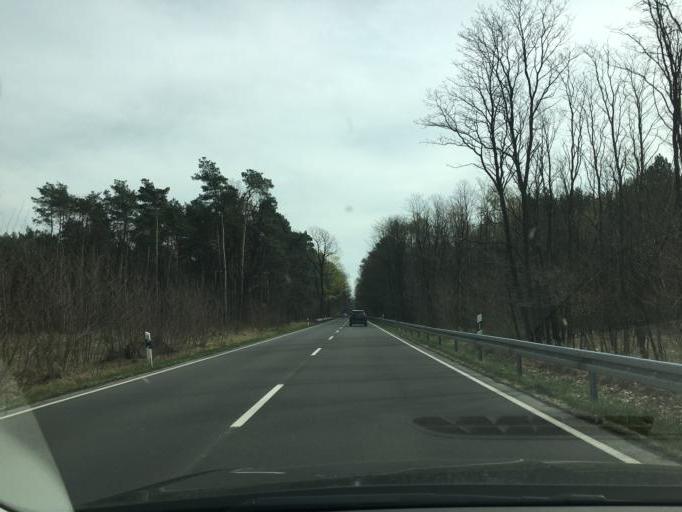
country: DE
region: Brandenburg
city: Spremberg
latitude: 51.5698
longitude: 14.4461
